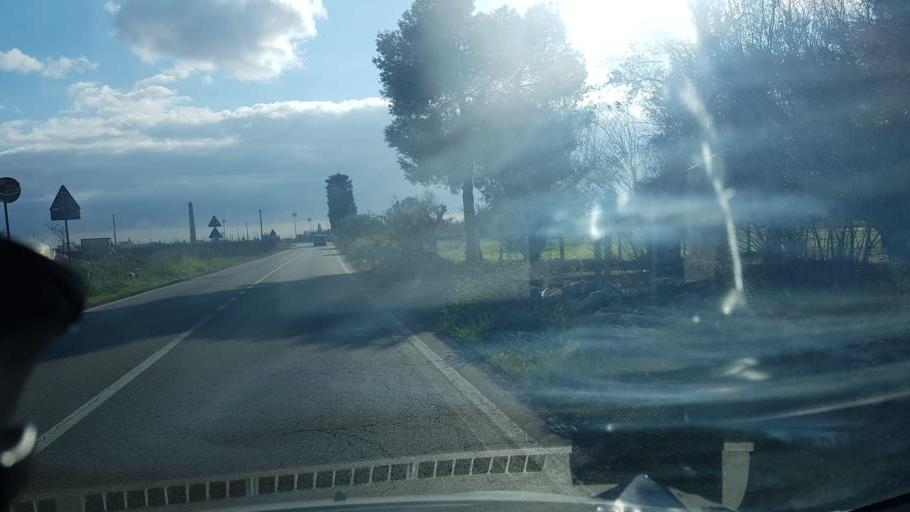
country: IT
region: Apulia
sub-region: Provincia di Lecce
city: Campi Salentina
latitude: 40.4109
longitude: 18.0236
